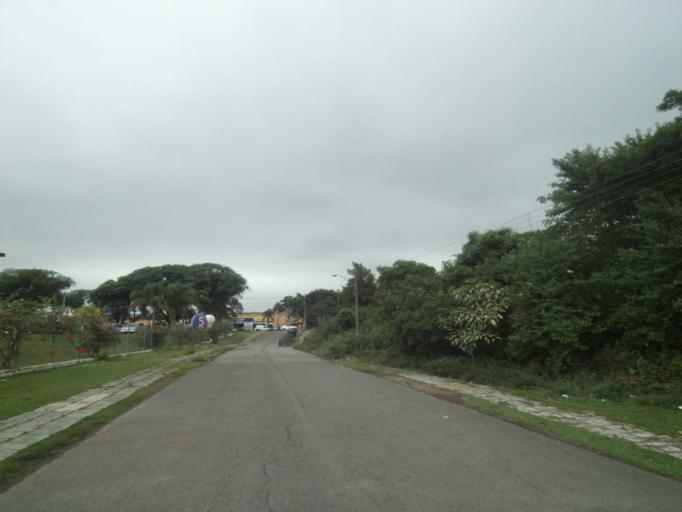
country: BR
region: Parana
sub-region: Curitiba
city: Curitiba
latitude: -25.4357
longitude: -49.3146
